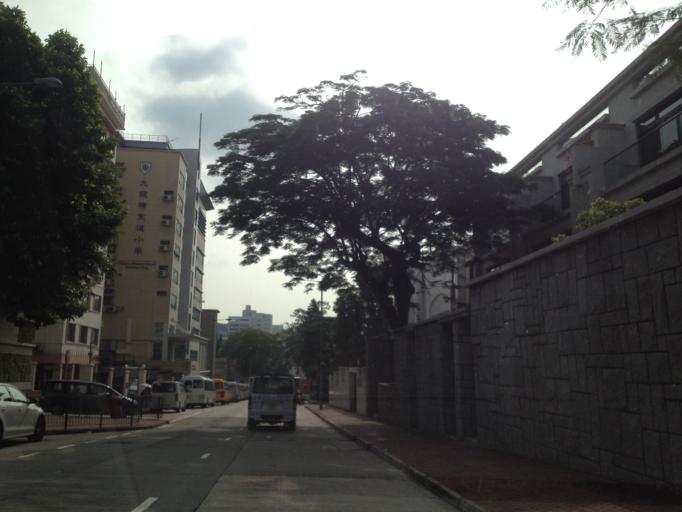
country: HK
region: Kowloon City
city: Kowloon
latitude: 22.3303
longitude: 114.1804
